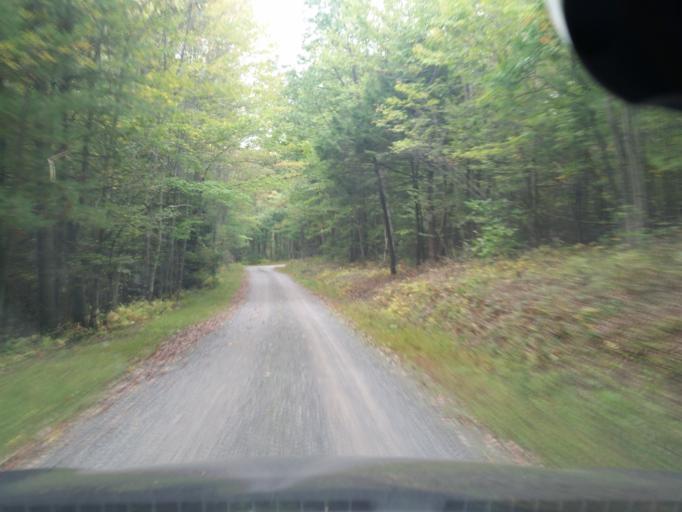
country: US
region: Pennsylvania
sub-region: Lycoming County
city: Jersey Shore
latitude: 41.0866
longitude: -77.2289
